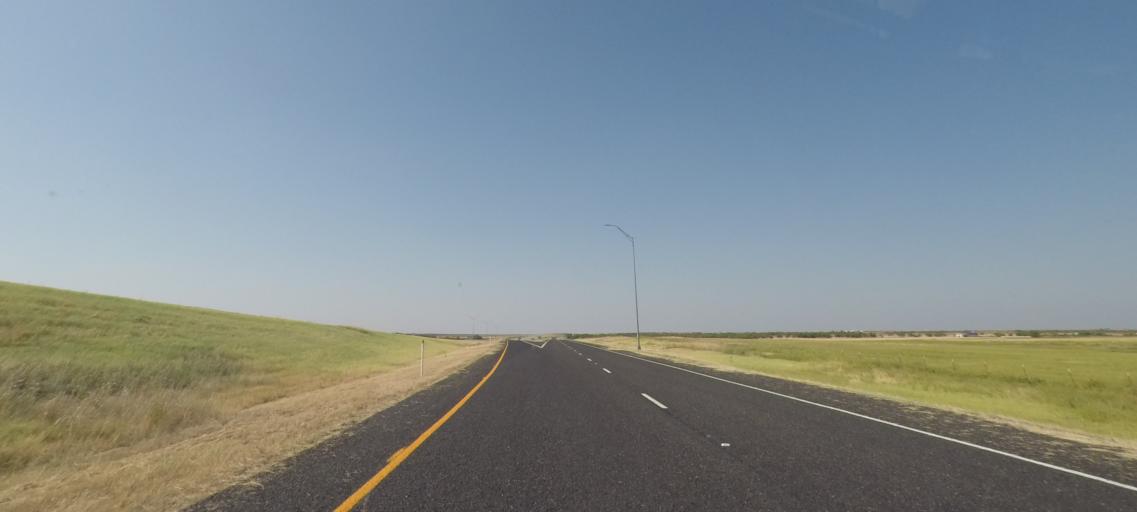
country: US
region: Texas
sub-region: Baylor County
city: Seymour
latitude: 33.5979
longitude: -99.2409
